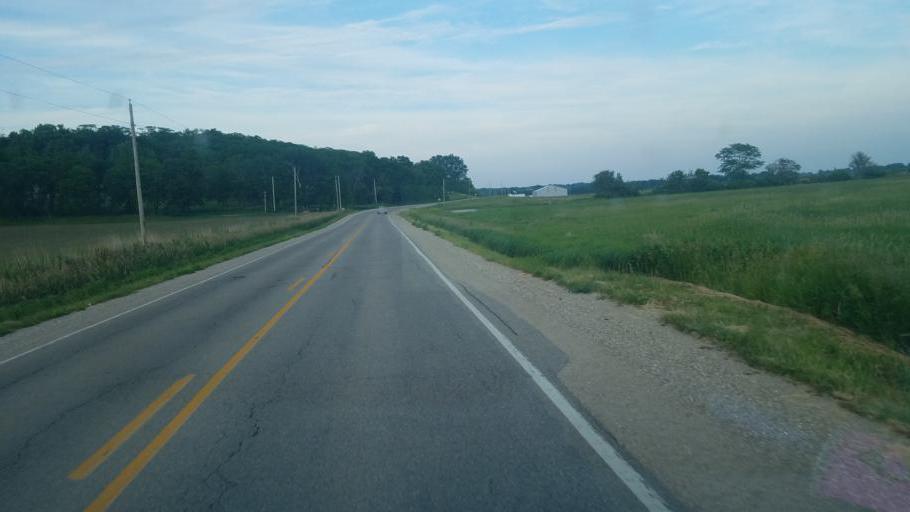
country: US
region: Iowa
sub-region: Benton County
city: Belle Plaine
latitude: 41.9203
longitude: -92.3779
